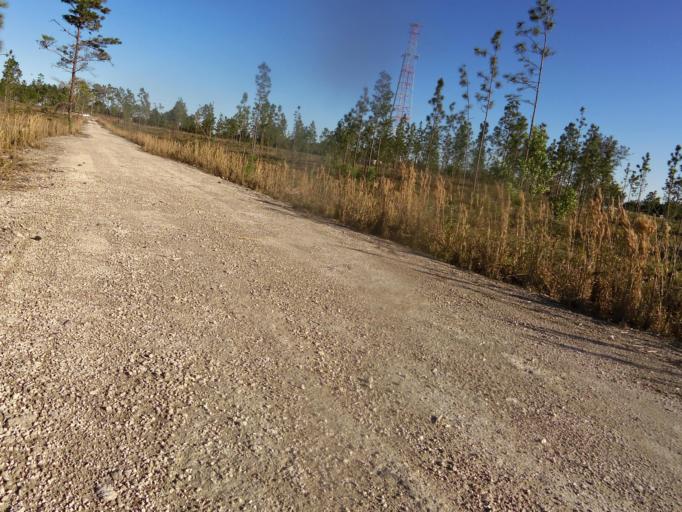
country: US
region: Florida
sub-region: Clay County
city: Keystone Heights
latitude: 29.8370
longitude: -81.9796
